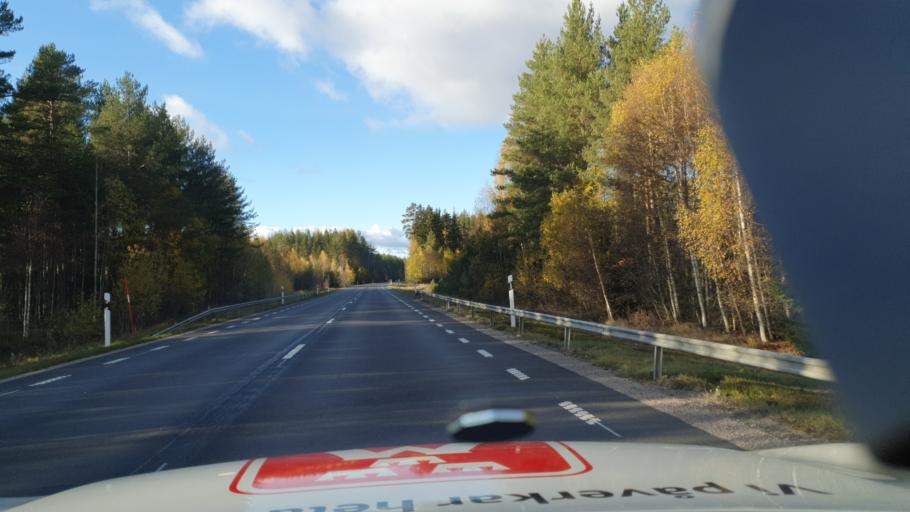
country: SE
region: Gaevleborg
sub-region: Gavle Kommun
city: Hedesunda
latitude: 60.4559
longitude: 16.9529
